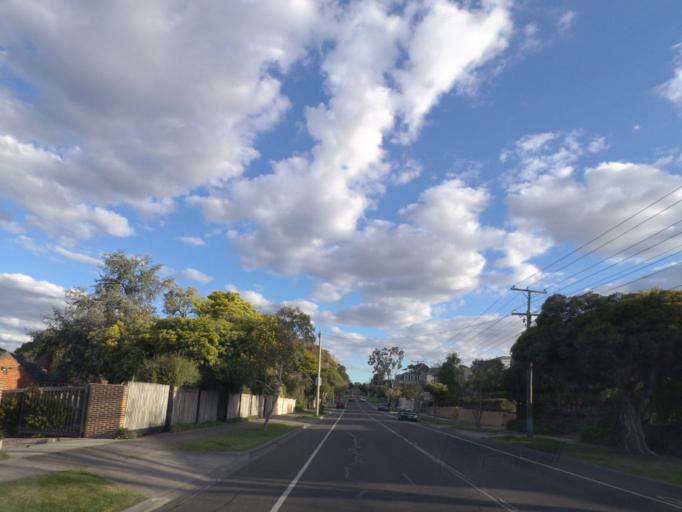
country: AU
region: Victoria
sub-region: Boroondara
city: Balwyn North
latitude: -37.7974
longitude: 145.0984
